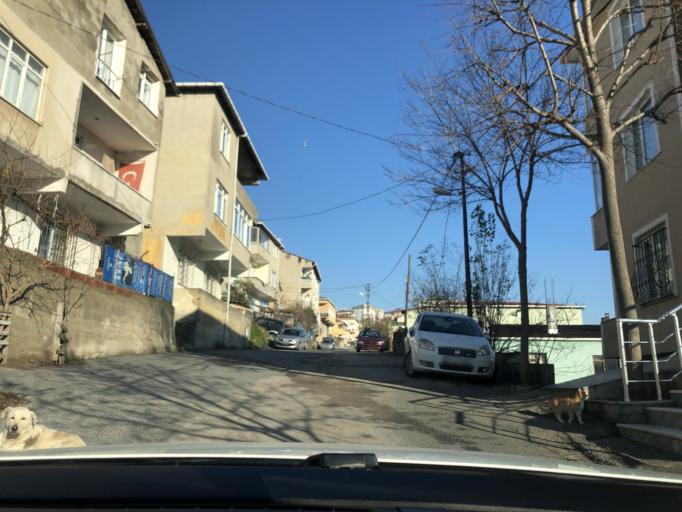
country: TR
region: Istanbul
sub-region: Atasehir
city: Atasehir
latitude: 40.9694
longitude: 29.1217
